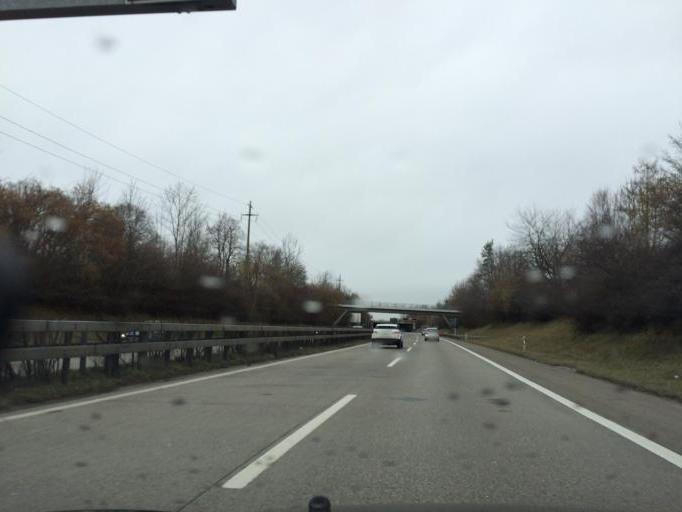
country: CH
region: Bern
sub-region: Thun District
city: Thun
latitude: 46.7474
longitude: 7.6028
